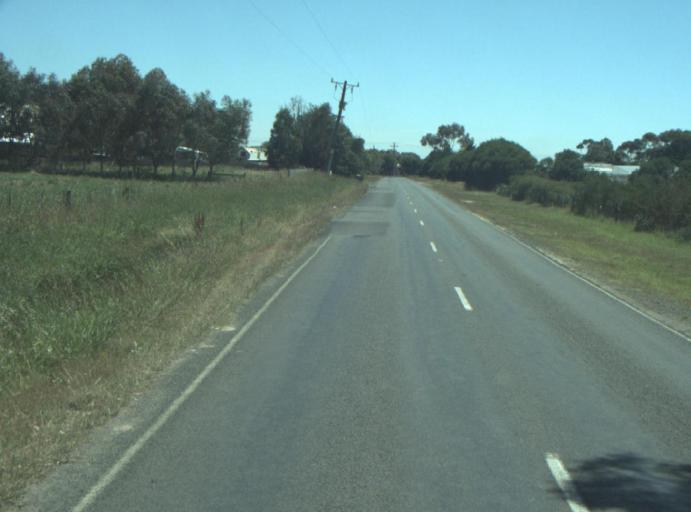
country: AU
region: Victoria
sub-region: Greater Geelong
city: Breakwater
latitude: -38.2102
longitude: 144.3586
